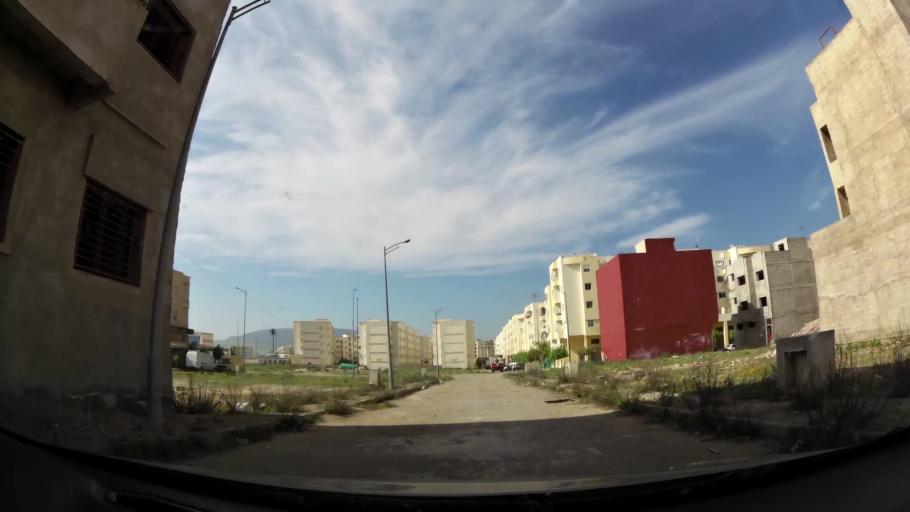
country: MA
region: Fes-Boulemane
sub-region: Fes
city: Fes
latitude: 34.0085
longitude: -5.0418
